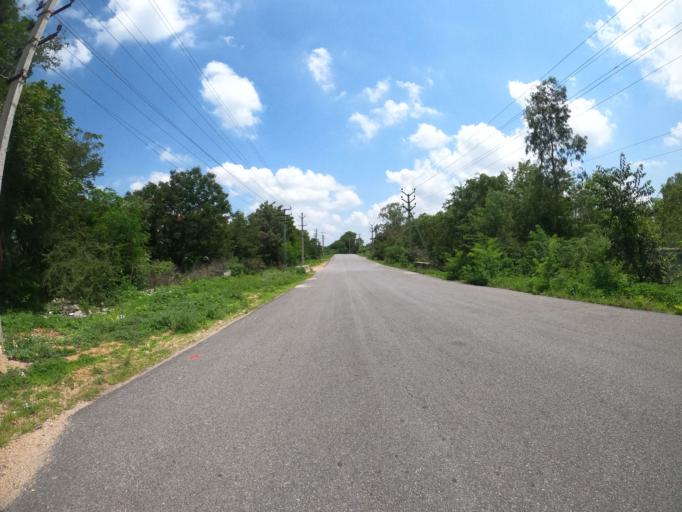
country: IN
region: Telangana
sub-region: Medak
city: Serilingampalle
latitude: 17.3927
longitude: 78.3135
